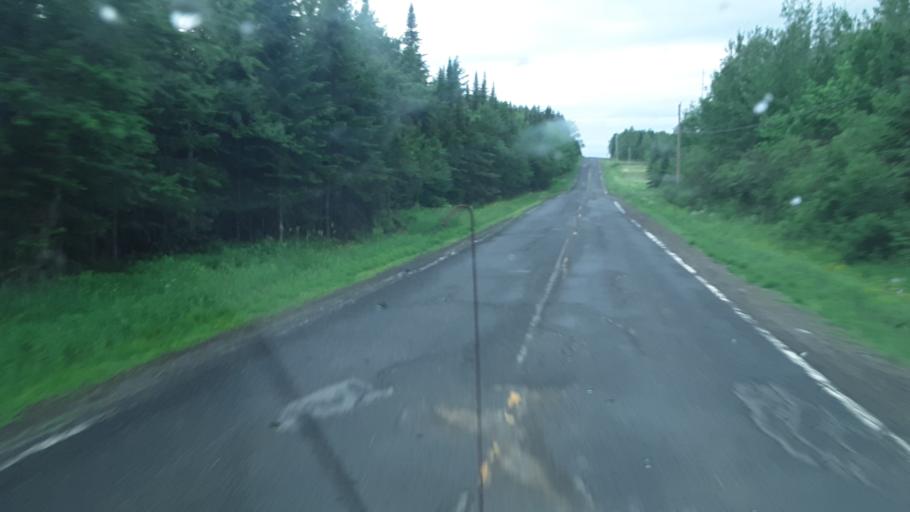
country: US
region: Maine
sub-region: Aroostook County
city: Caribou
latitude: 46.8788
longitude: -68.2051
